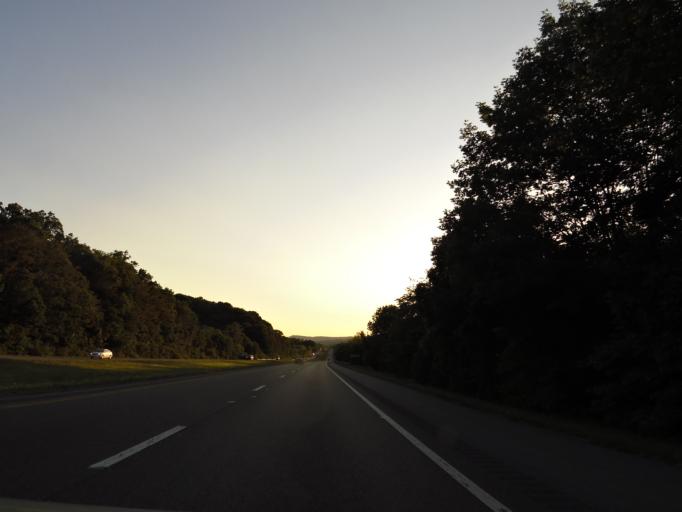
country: US
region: Tennessee
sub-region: Washington County
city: Fall Branch
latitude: 36.3556
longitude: -82.7165
